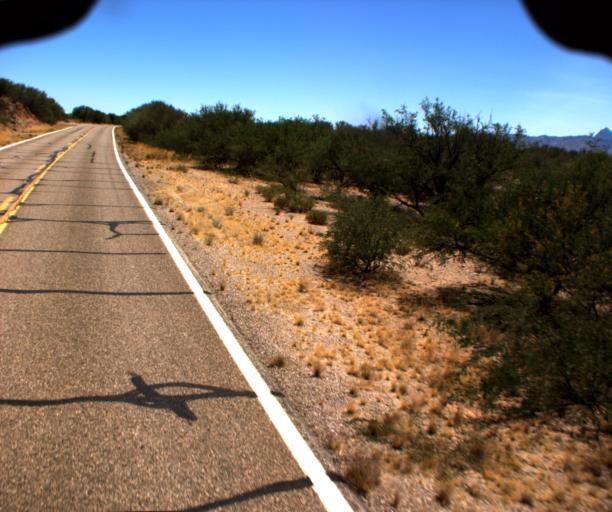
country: US
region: Arizona
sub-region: Pima County
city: Three Points
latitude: 31.8896
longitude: -111.3934
